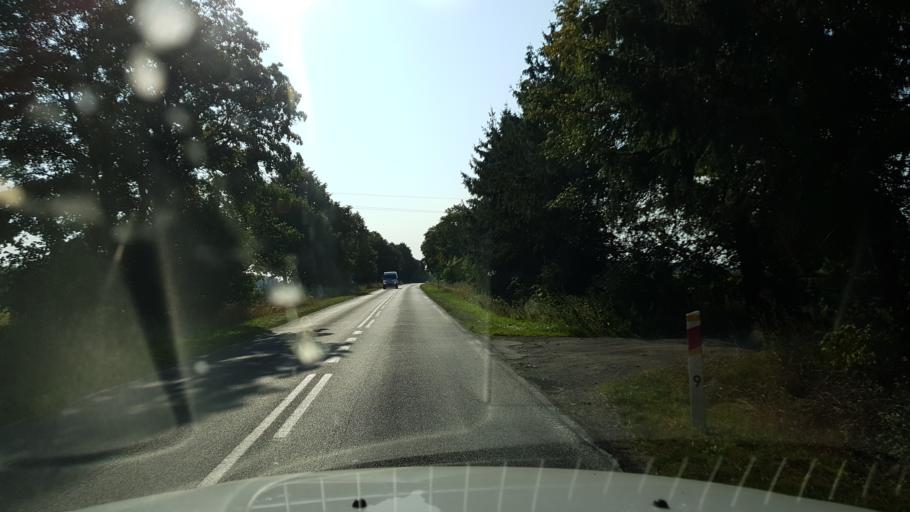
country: PL
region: West Pomeranian Voivodeship
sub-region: Powiat gryficki
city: Ploty
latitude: 53.7967
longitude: 15.2770
